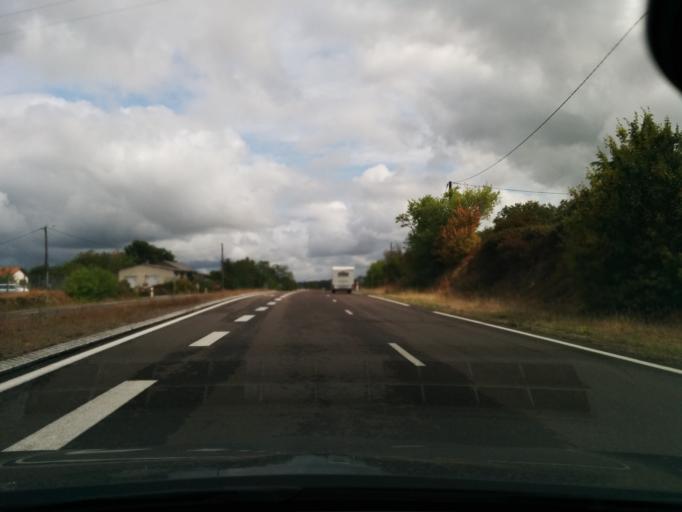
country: FR
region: Midi-Pyrenees
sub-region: Departement du Lot
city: Souillac
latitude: 44.9243
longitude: 1.4916
